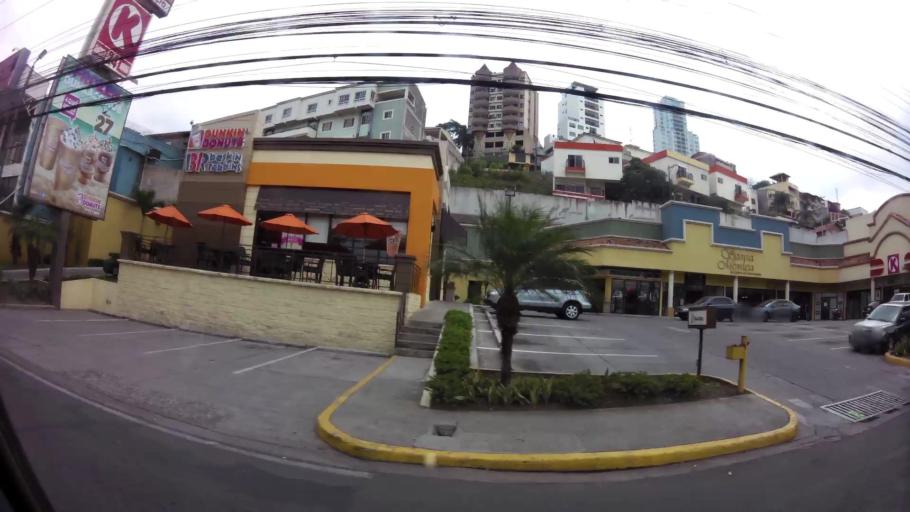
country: HN
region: Francisco Morazan
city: Tegucigalpa
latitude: 14.0894
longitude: -87.1888
